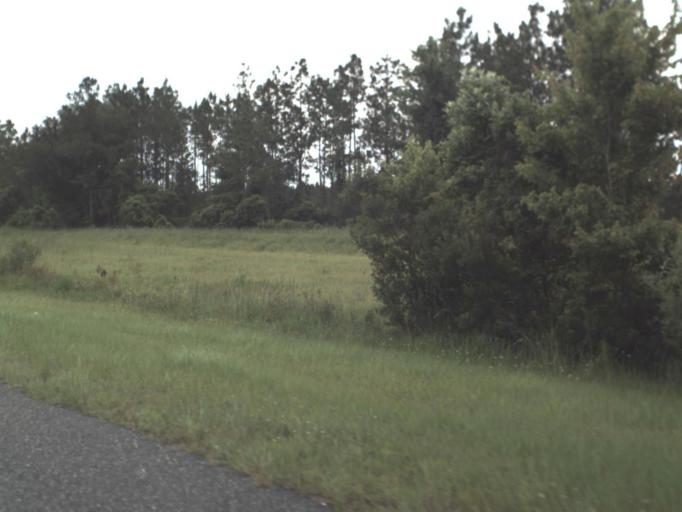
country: US
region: Florida
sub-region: Levy County
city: Bronson
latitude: 29.3158
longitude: -82.7613
